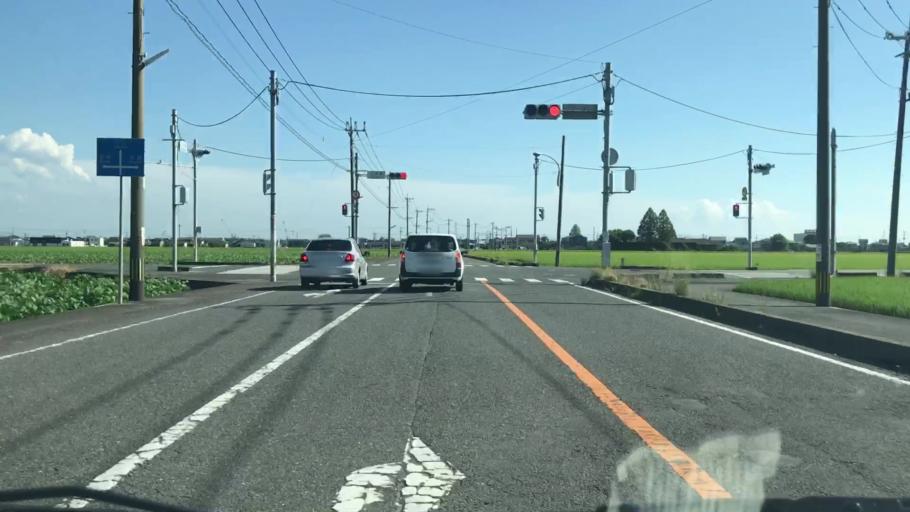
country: JP
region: Saga Prefecture
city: Okawa
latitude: 33.2209
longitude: 130.3508
